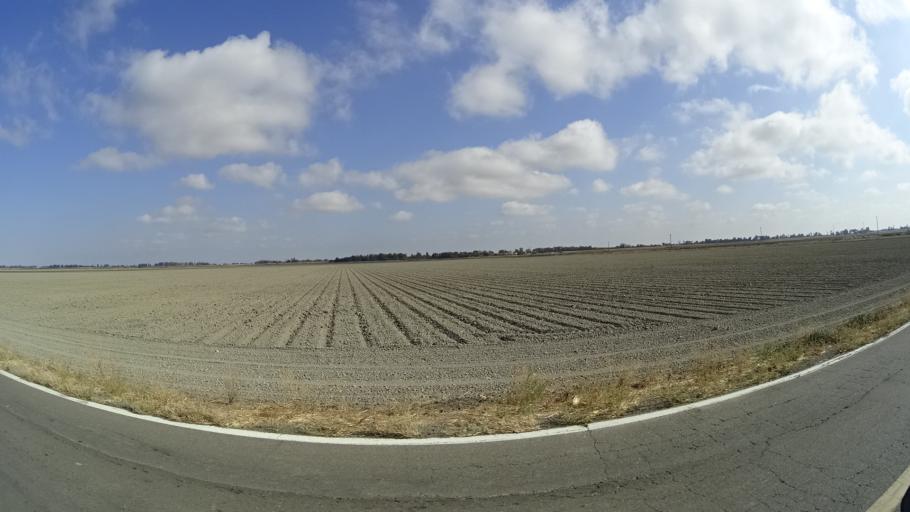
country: US
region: California
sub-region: Yolo County
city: Woodland
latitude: 38.8287
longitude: -121.7484
